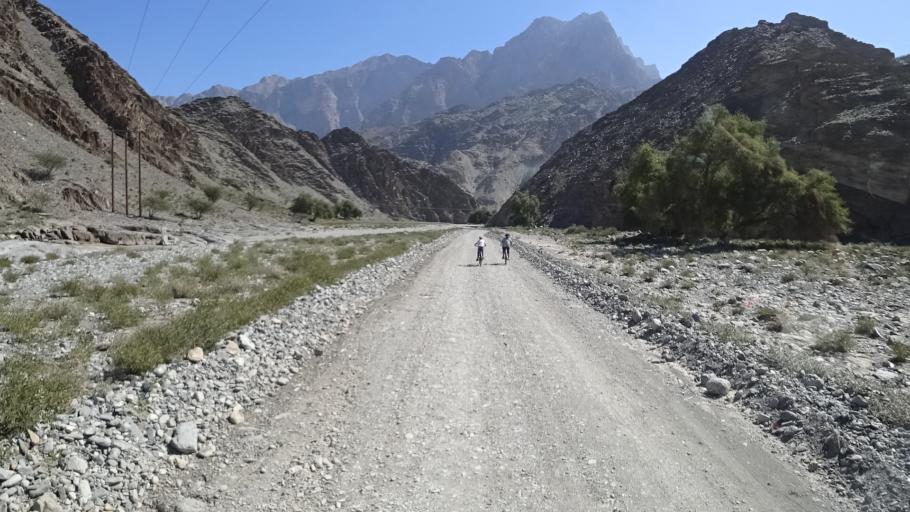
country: OM
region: Al Batinah
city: Bayt al `Awabi
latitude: 23.2598
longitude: 57.4362
